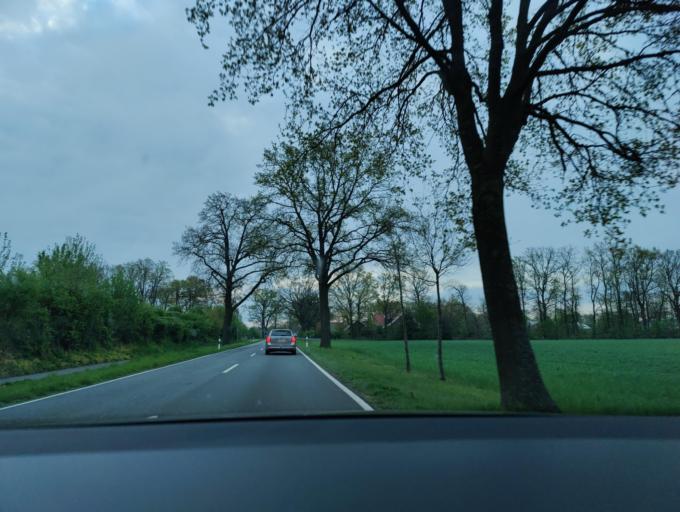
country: DE
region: Lower Saxony
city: Wietmarschen
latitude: 52.4923
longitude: 7.2182
